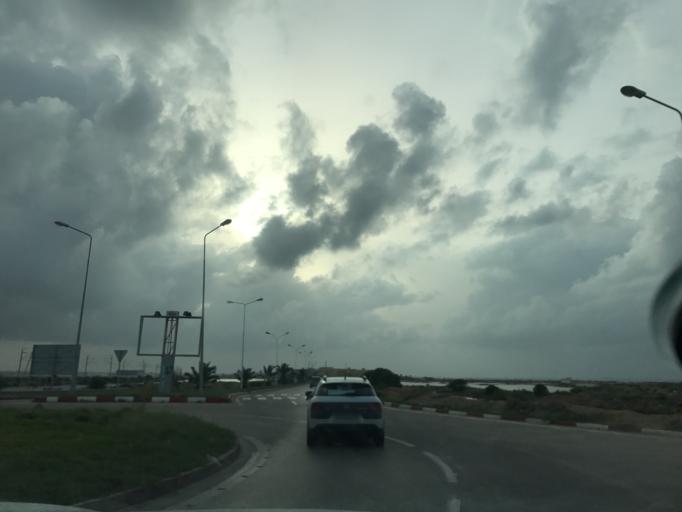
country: TN
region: Al Munastir
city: Saqanis
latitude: 35.7723
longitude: 10.7772
